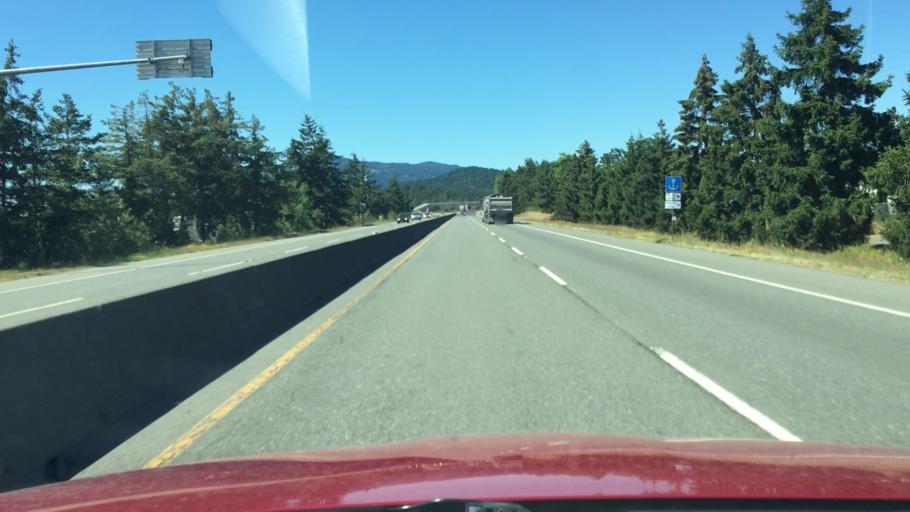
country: CA
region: British Columbia
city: North Saanich
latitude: 48.6571
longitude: -123.4130
